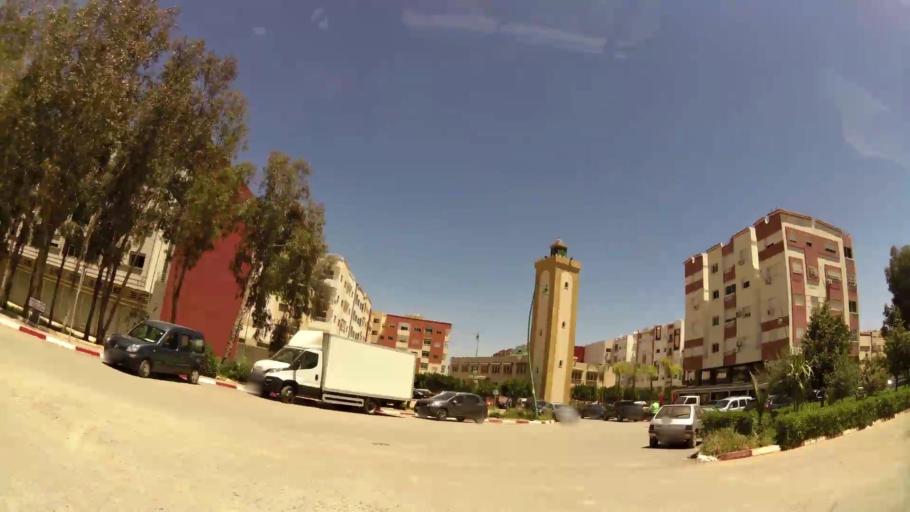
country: MA
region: Meknes-Tafilalet
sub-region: Meknes
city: Meknes
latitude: 33.8539
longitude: -5.5686
